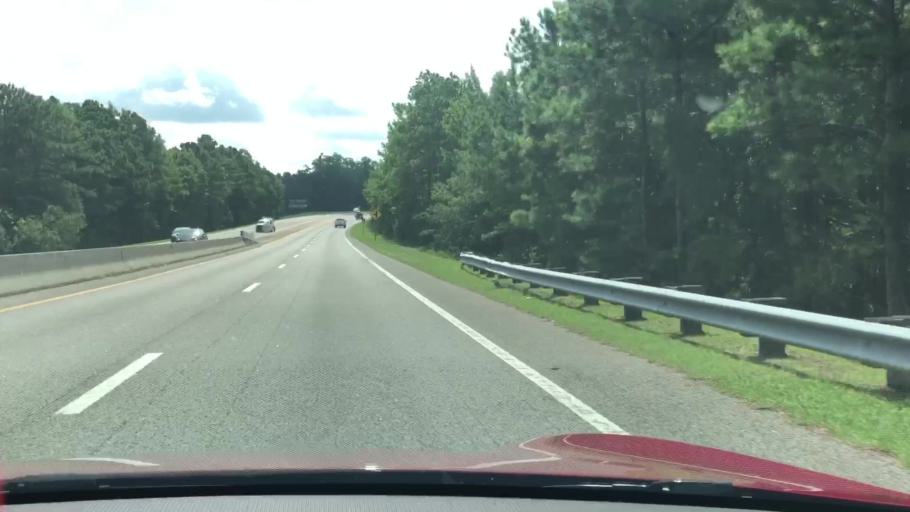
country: US
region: North Carolina
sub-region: Currituck County
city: Currituck
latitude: 36.3375
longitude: -75.9506
